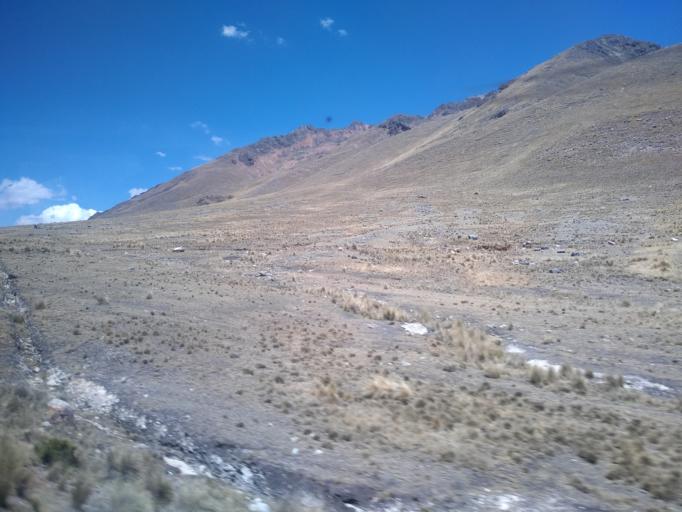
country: PE
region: Cusco
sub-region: Provincia de Canas
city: Layo
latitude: -14.4813
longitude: -71.0014
